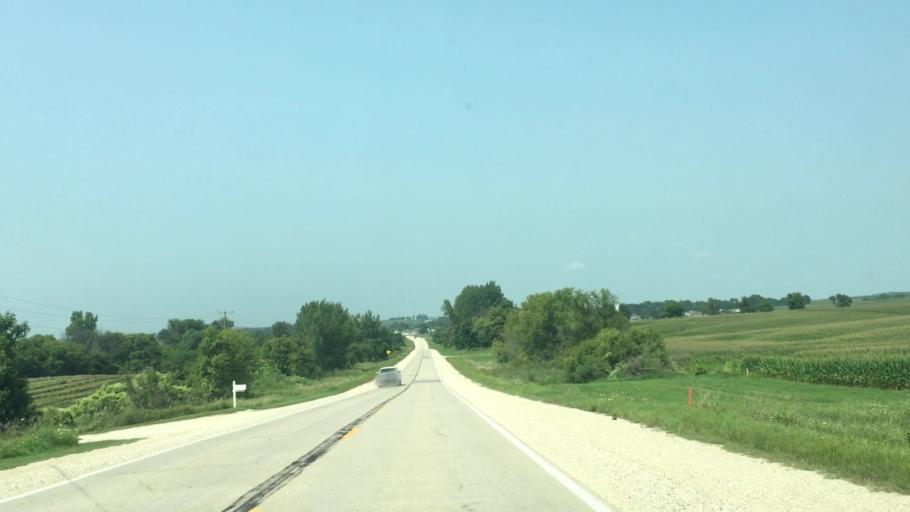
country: US
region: Iowa
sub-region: Fayette County
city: West Union
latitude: 43.1073
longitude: -91.8691
